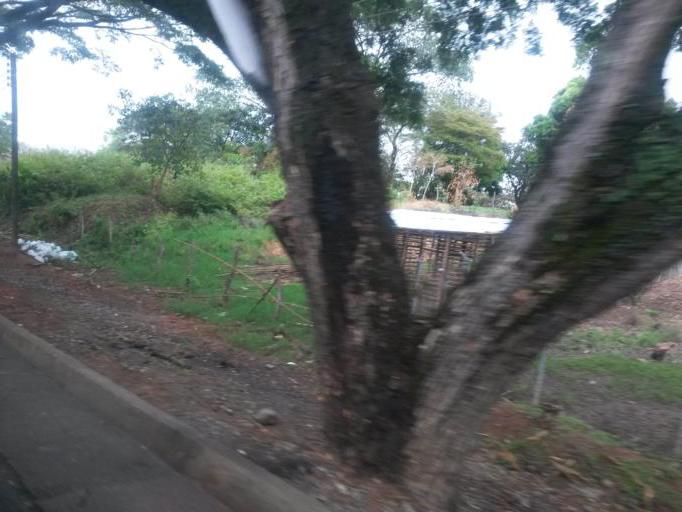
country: CO
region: Cauca
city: El Bordo
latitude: 2.1704
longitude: -76.8993
